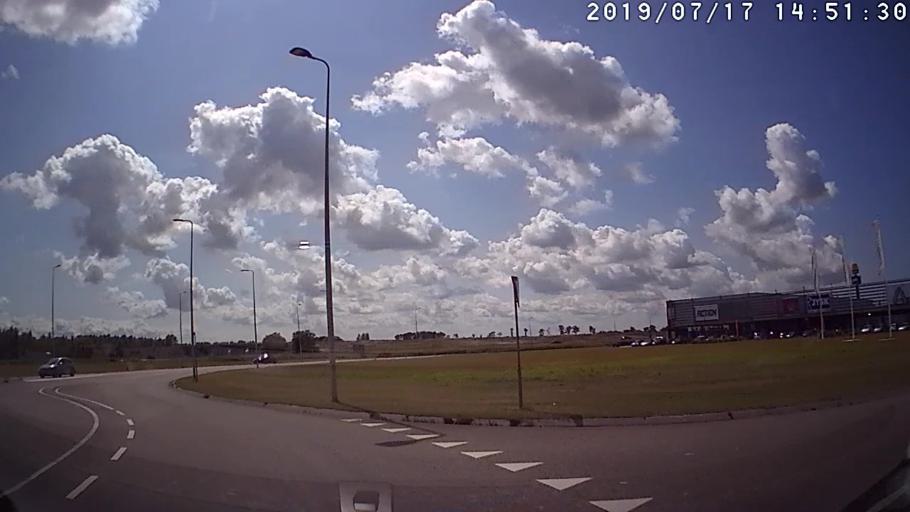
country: NL
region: Overijssel
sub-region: Gemeente Kampen
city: Kampen
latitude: 52.5571
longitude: 5.8847
